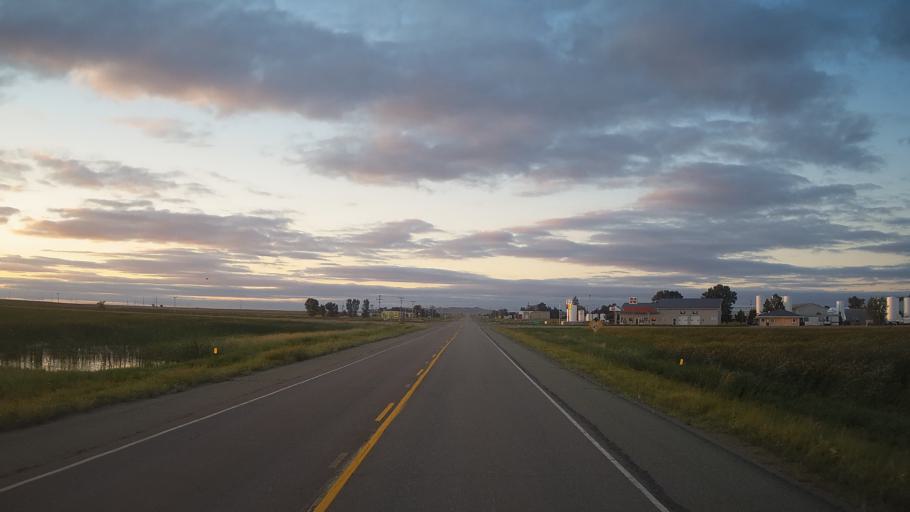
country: US
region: South Dakota
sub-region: Buffalo County
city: Fort Thompson
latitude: 43.8736
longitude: -99.6060
